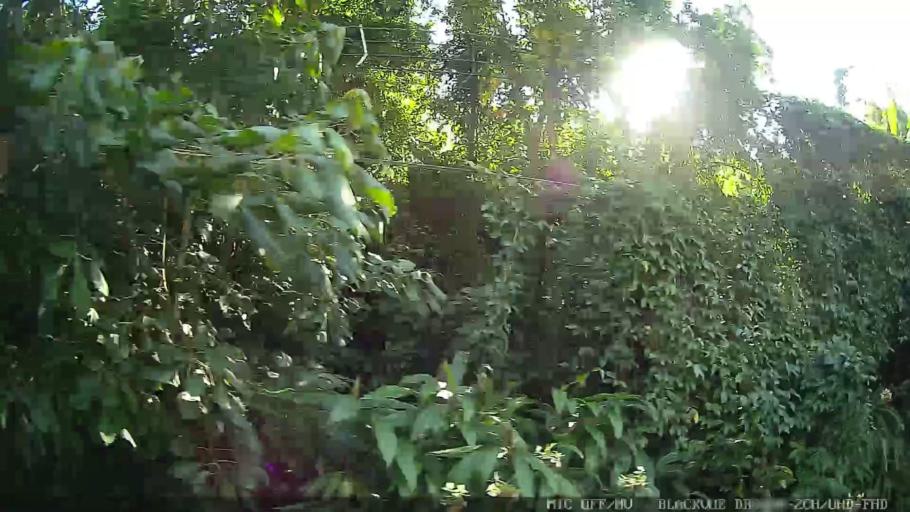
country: BR
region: Sao Paulo
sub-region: Guaruja
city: Guaruja
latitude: -24.0119
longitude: -46.2815
